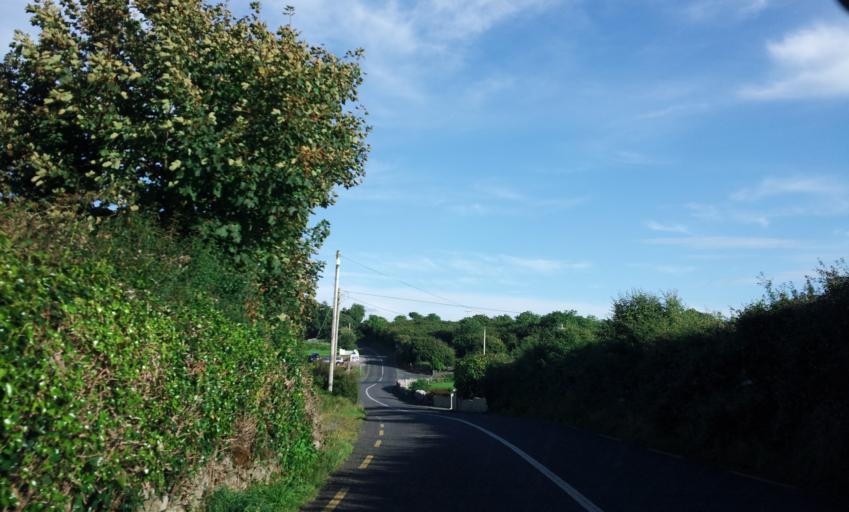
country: IE
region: Munster
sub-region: An Clar
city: Ennis
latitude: 52.9753
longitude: -9.0992
